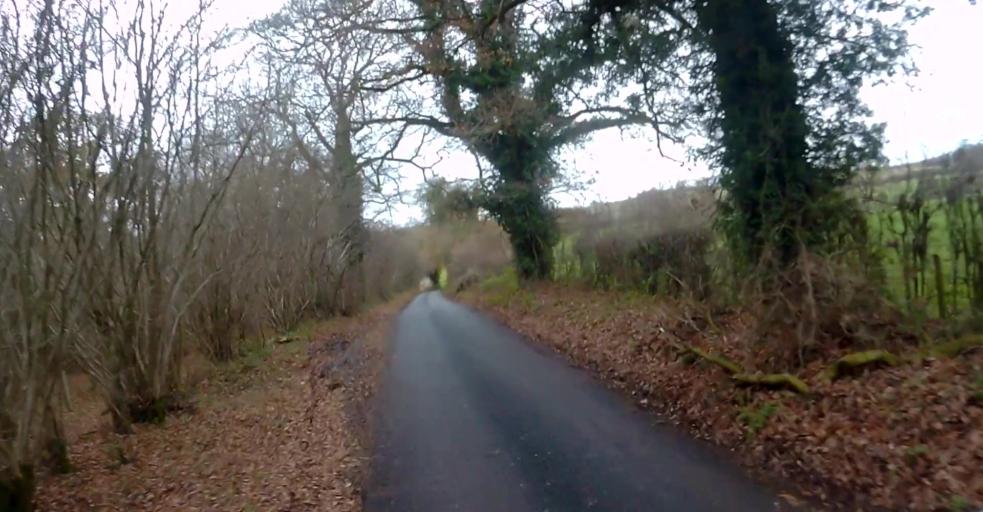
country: GB
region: England
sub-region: Hampshire
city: Overton
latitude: 51.2221
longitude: -1.2275
